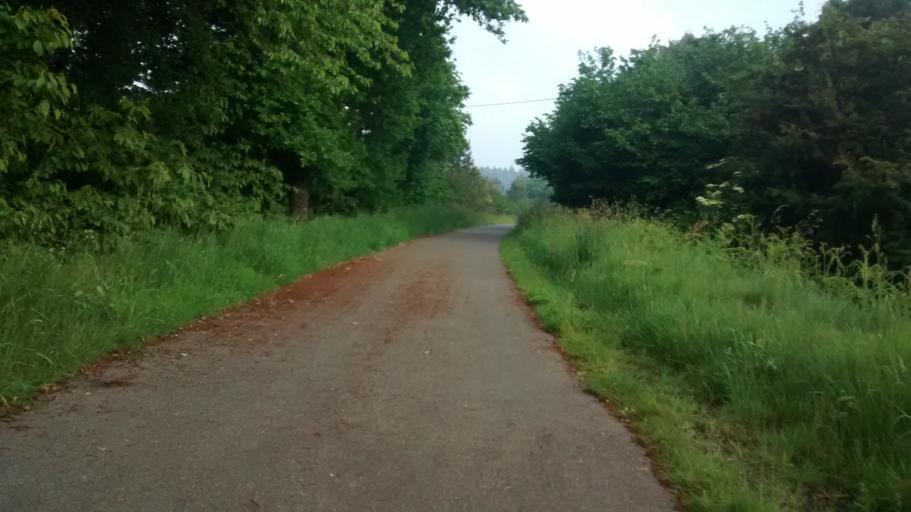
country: FR
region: Brittany
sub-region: Departement du Morbihan
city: Malestroit
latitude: 47.7901
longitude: -2.4036
